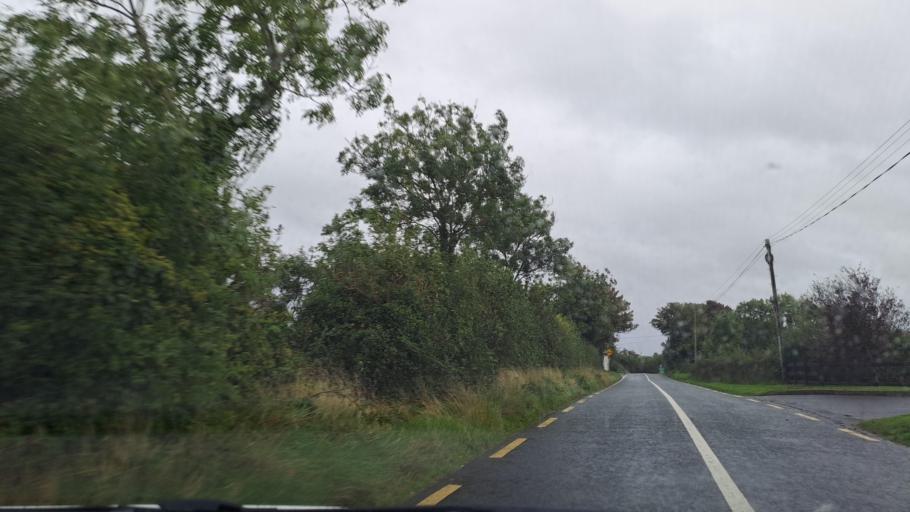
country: IE
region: Leinster
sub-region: Lu
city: Dromiskin
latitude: 53.9591
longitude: -6.4510
